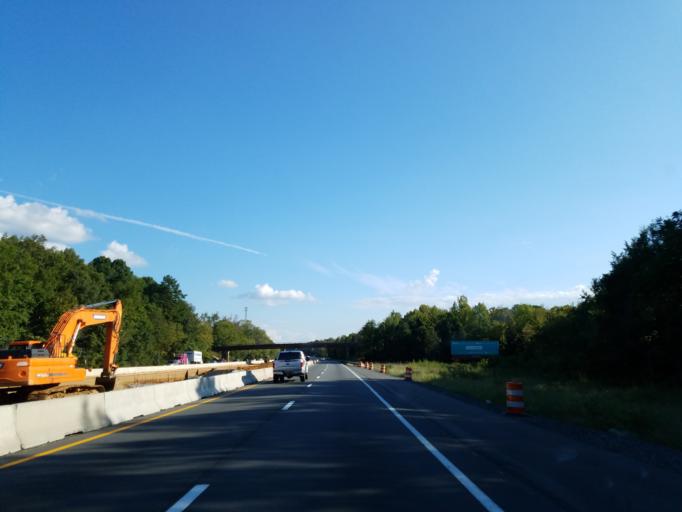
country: US
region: North Carolina
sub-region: Rowan County
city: Landis
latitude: 35.5280
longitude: -80.5732
